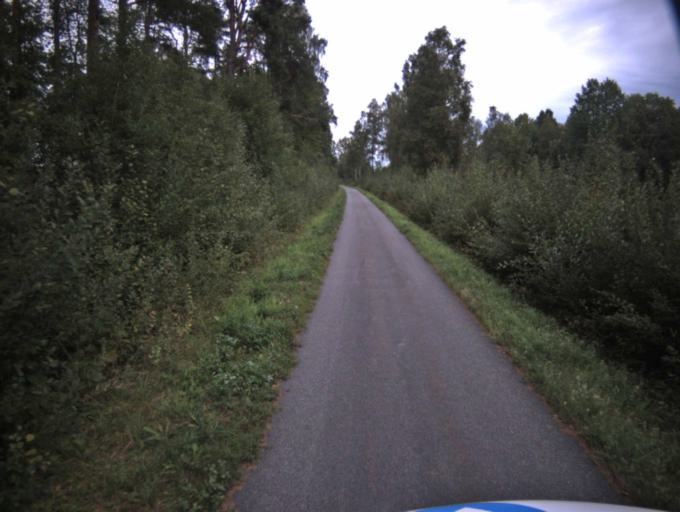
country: SE
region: Vaestra Goetaland
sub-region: Ulricehamns Kommun
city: Ulricehamn
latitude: 57.9518
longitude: 13.5067
